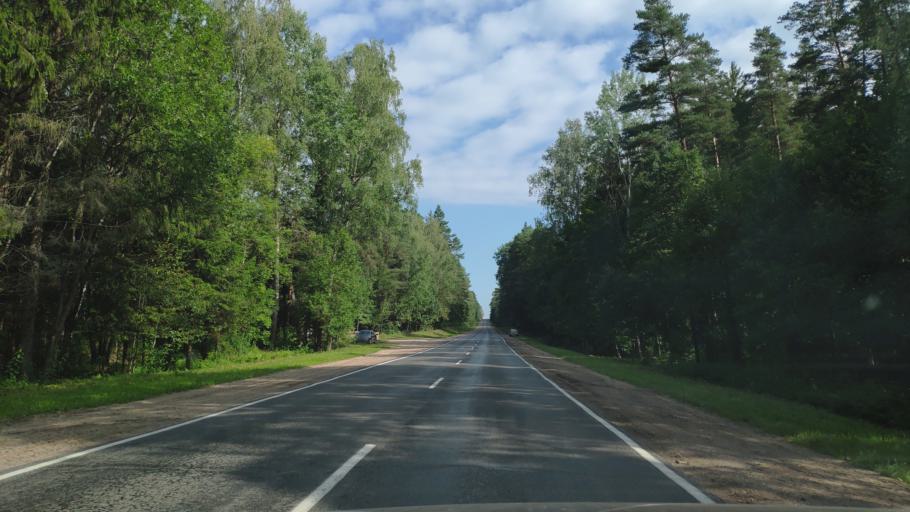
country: BY
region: Minsk
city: Novosel'ye
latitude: 53.9356
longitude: 27.2439
